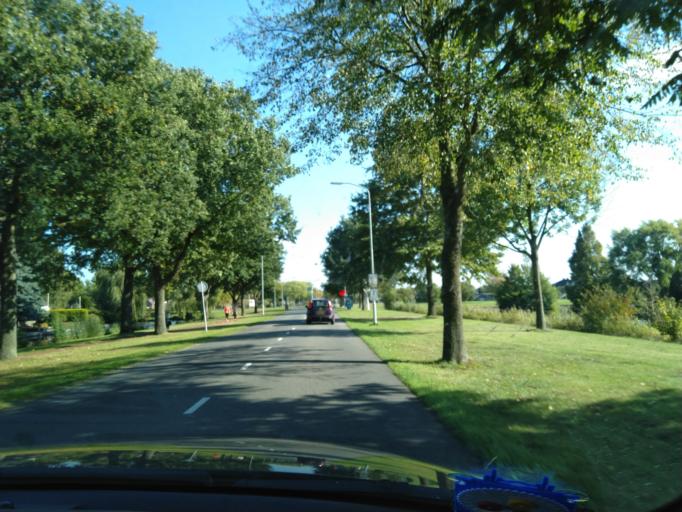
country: NL
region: Groningen
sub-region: Gemeente Veendam
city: Veendam
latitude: 53.0893
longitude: 6.8504
